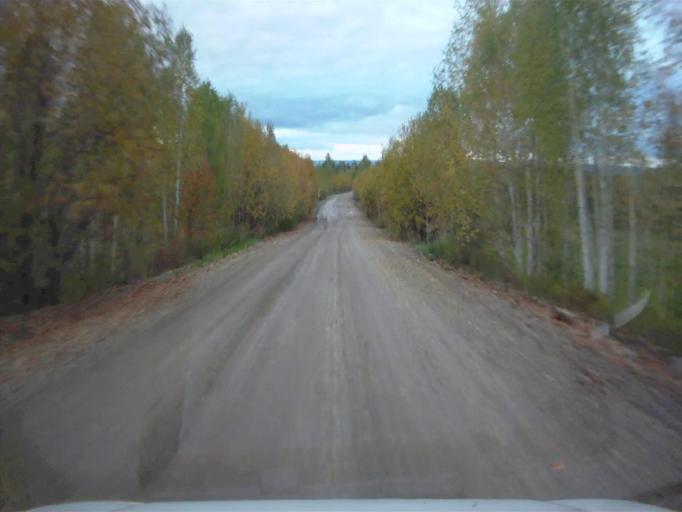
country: RU
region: Sverdlovsk
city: Mikhaylovsk
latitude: 56.2050
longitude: 59.2035
